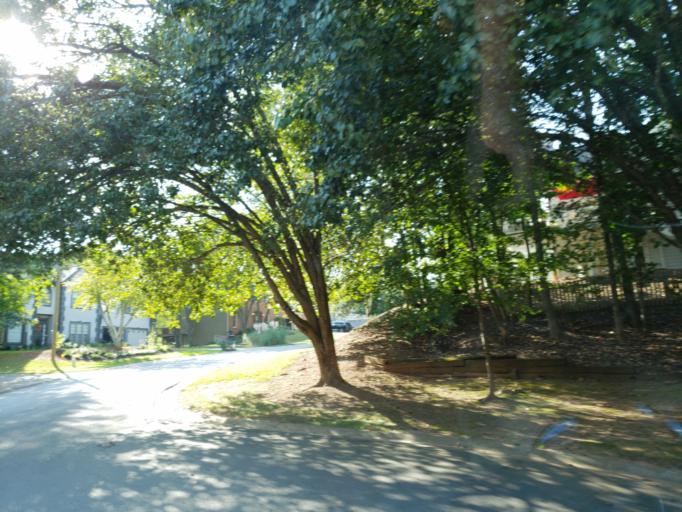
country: US
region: Georgia
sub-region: Cherokee County
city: Woodstock
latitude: 34.0573
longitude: -84.4459
